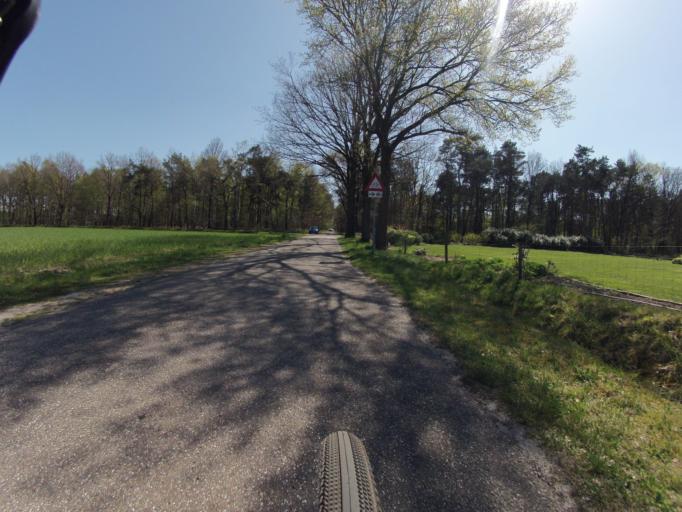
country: NL
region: Overijssel
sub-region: Gemeente Losser
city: Losser
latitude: 52.2662
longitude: 6.9766
